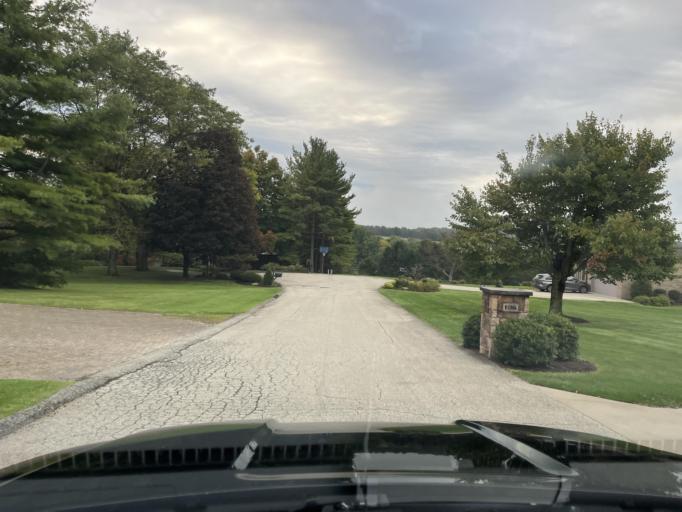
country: US
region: Pennsylvania
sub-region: Fayette County
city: Leith-Hatfield
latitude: 39.8745
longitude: -79.7228
